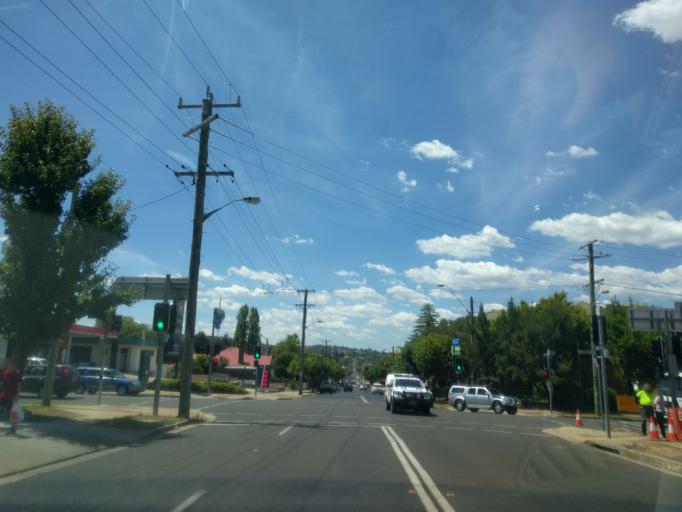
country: AU
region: New South Wales
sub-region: Armidale Dumaresq
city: Armidale
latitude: -30.5176
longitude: 151.6677
